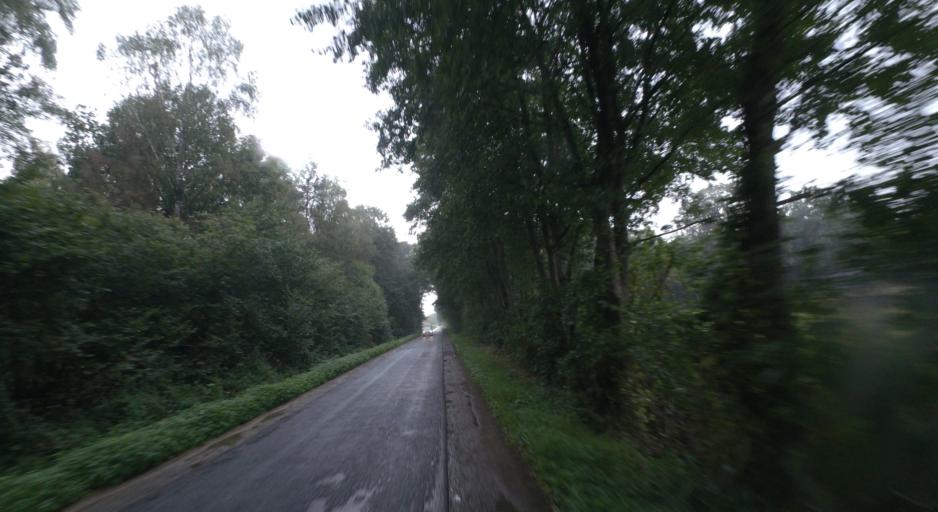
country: DE
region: North Rhine-Westphalia
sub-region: Regierungsbezirk Dusseldorf
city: Wesel
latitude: 51.7059
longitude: 6.6219
